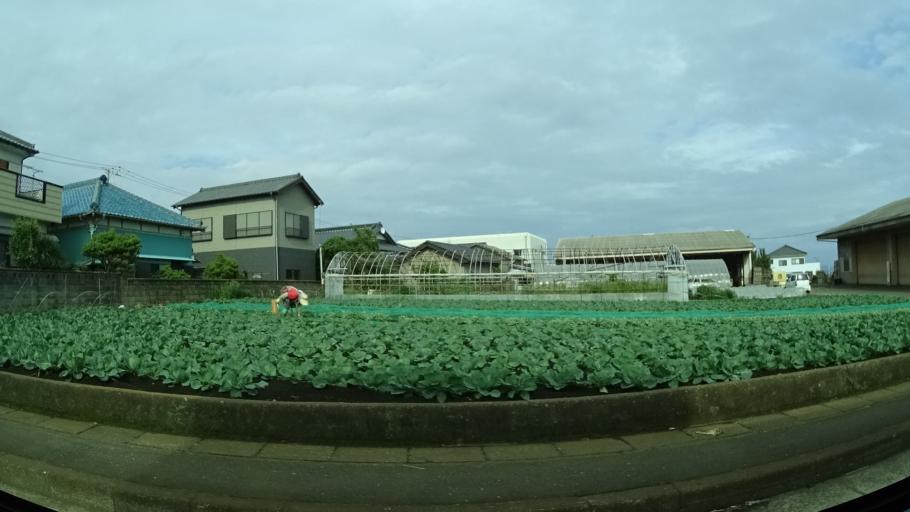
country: JP
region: Kanagawa
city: Miura
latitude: 35.1512
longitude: 139.6688
